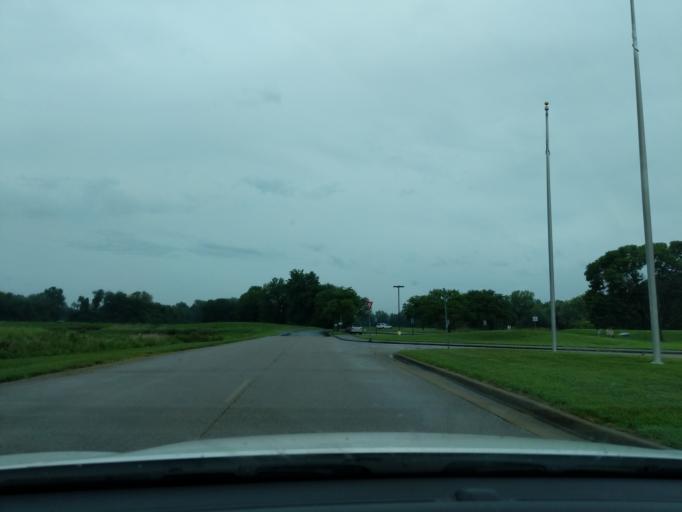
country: US
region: Illinois
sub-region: Saint Clair County
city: Fairmont City
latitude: 38.6549
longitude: -90.0586
